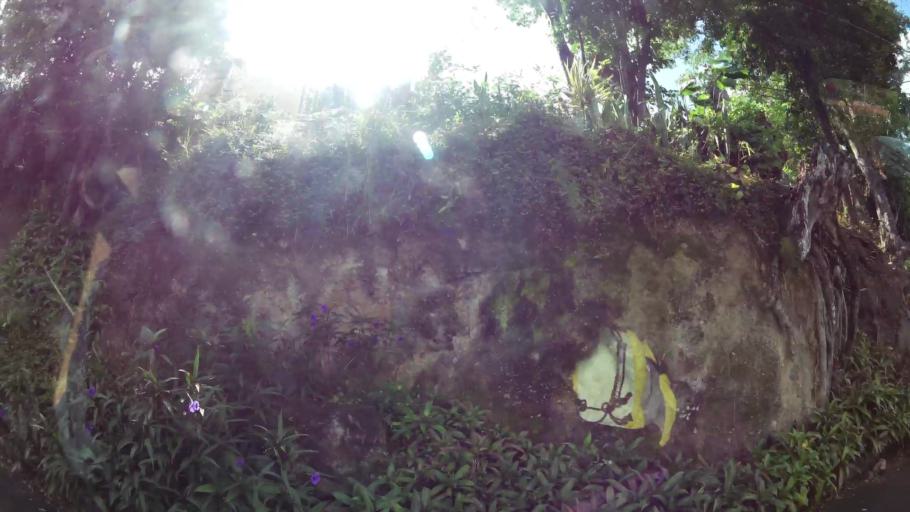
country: MQ
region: Martinique
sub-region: Martinique
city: Les Trois-Ilets
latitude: 14.4814
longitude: -61.0164
